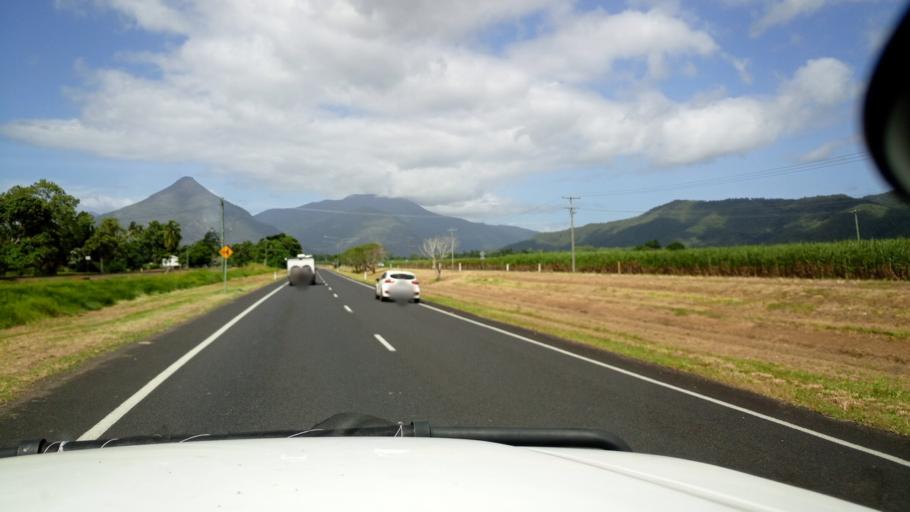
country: AU
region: Queensland
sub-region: Cairns
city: Woree
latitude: -17.0640
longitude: 145.7711
